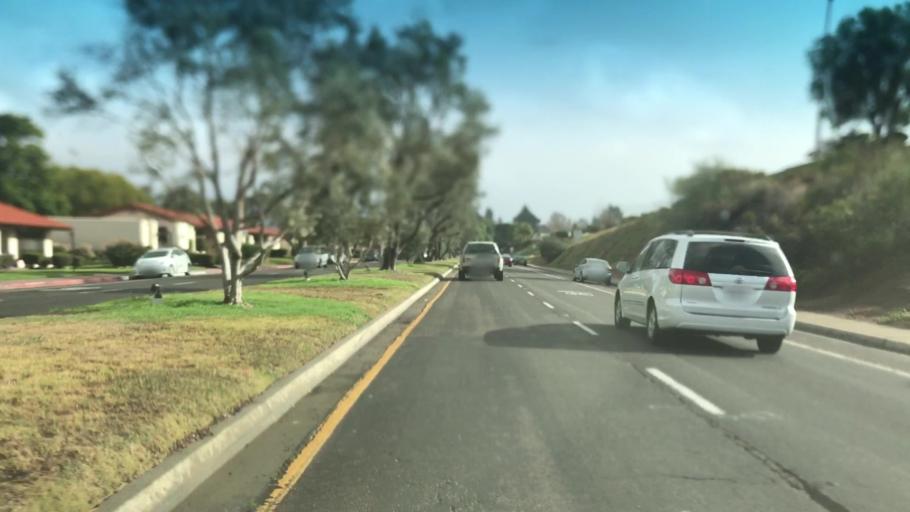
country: US
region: California
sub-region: San Diego County
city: Poway
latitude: 33.0214
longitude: -117.0683
